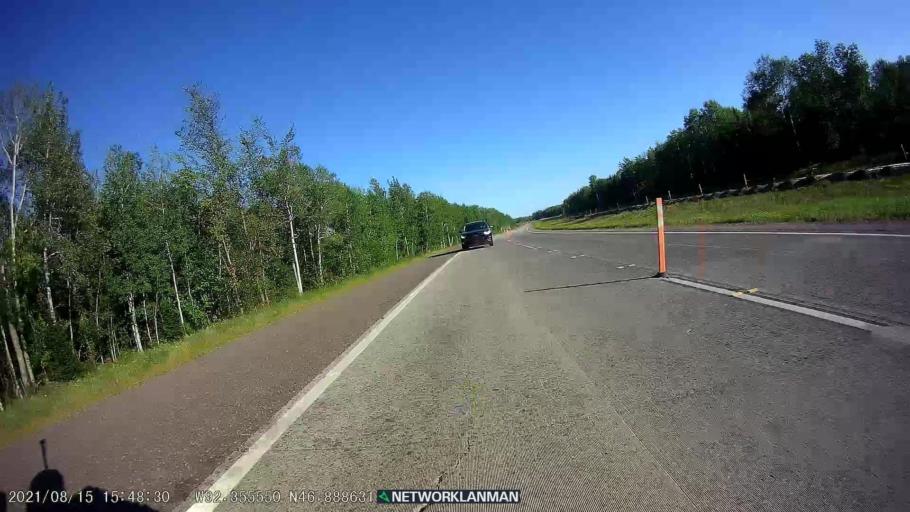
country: US
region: Minnesota
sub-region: Saint Louis County
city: Hermantown
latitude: 46.8889
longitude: -92.3555
